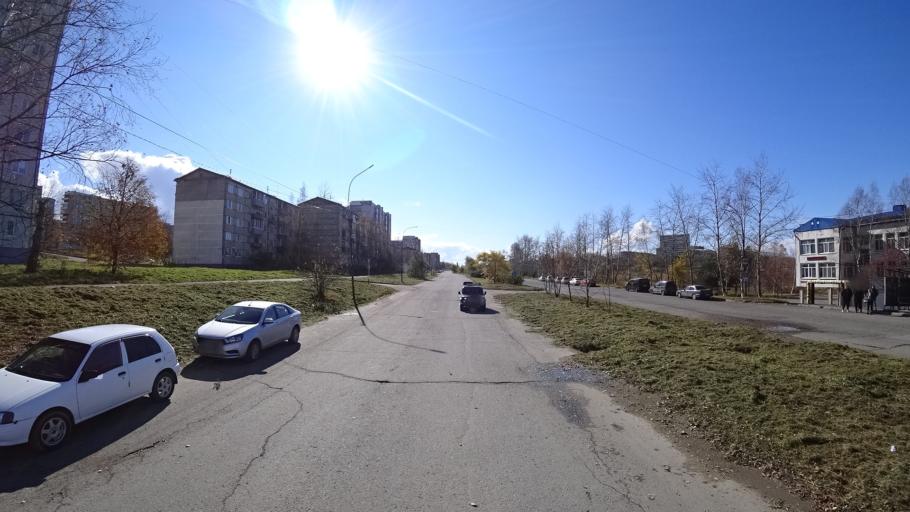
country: RU
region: Khabarovsk Krai
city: Amursk
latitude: 50.2472
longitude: 136.9166
